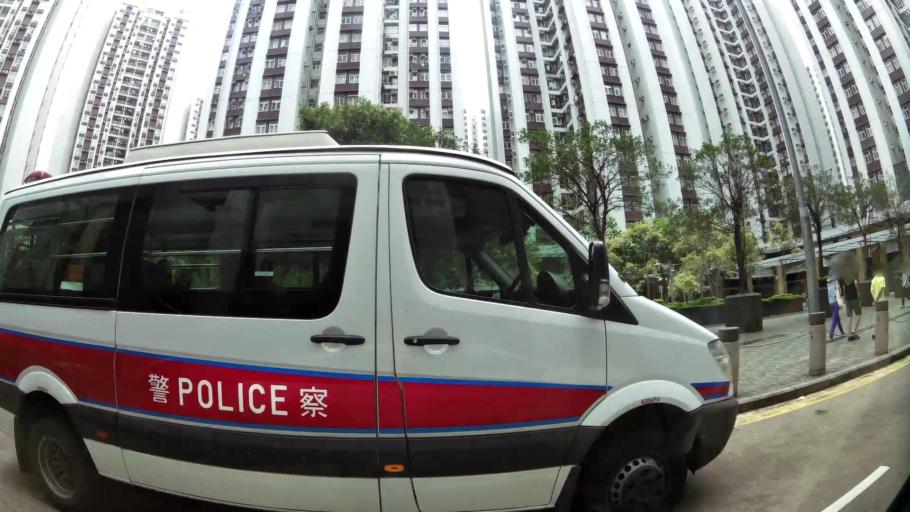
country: HK
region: Kowloon City
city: Kowloon
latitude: 22.2871
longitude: 114.2183
